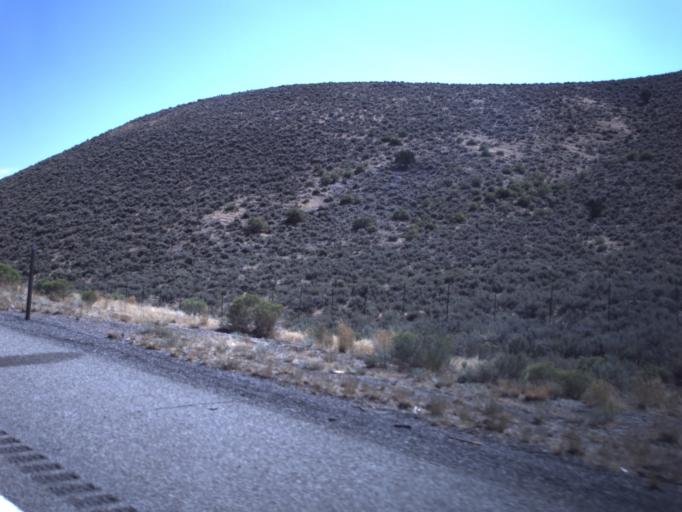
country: US
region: Utah
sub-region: Sevier County
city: Aurora
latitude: 38.8791
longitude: -111.9293
